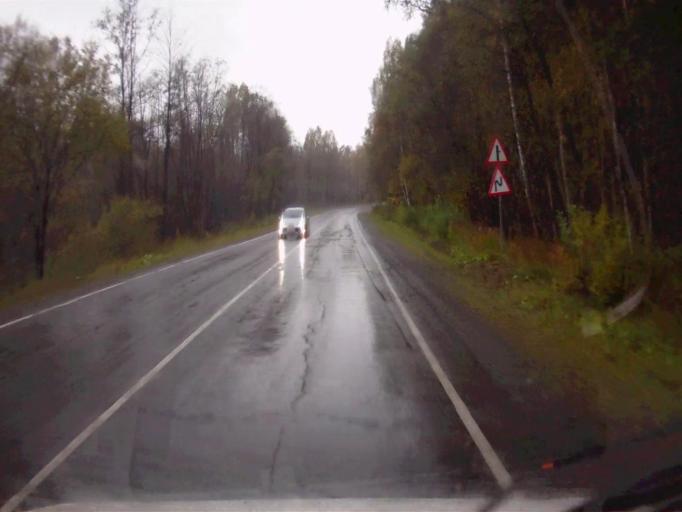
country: RU
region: Chelyabinsk
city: Kyshtym
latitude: 55.9059
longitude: 60.4421
